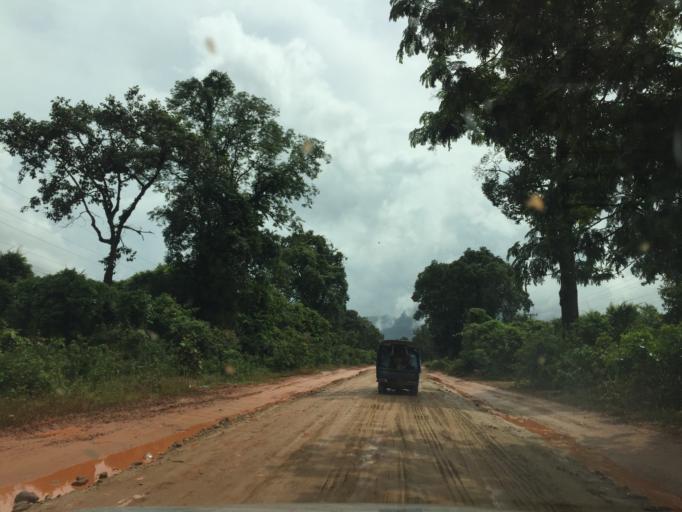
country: LA
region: Attapu
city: Attapu
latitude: 14.8095
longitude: 106.7769
